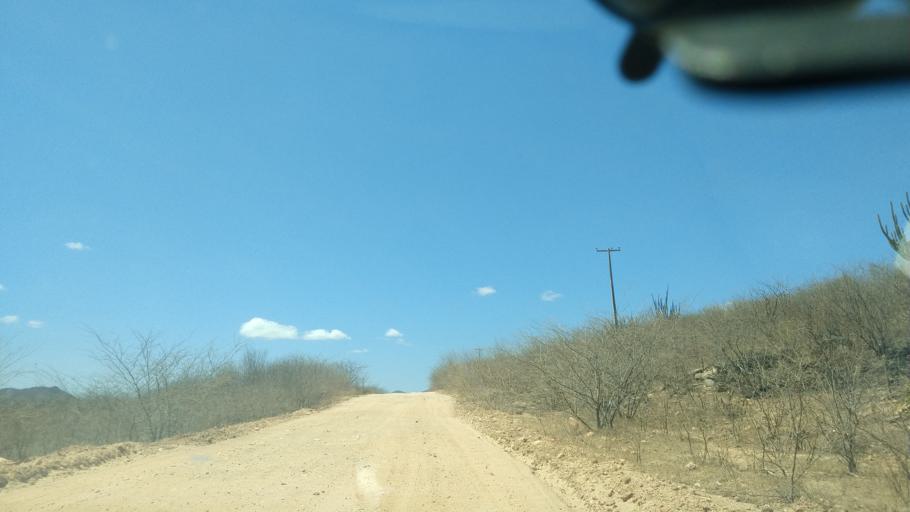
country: BR
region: Rio Grande do Norte
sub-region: Sao Tome
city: Sao Tome
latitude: -5.9718
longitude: -36.1639
